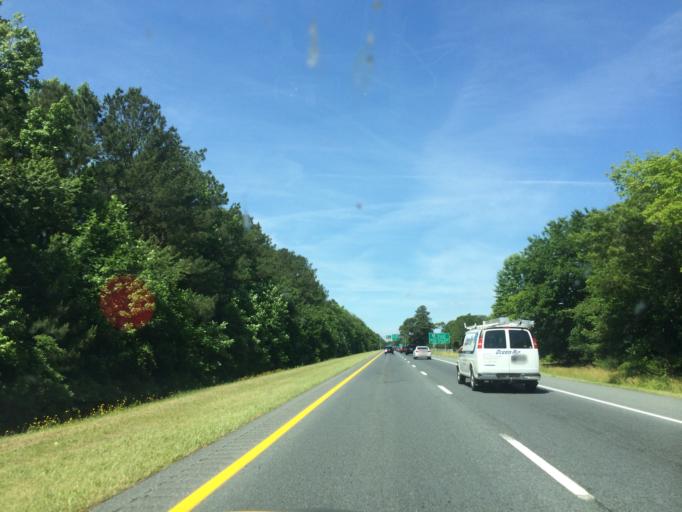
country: US
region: Maryland
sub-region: Wicomico County
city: Salisbury
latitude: 38.3744
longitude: -75.5119
